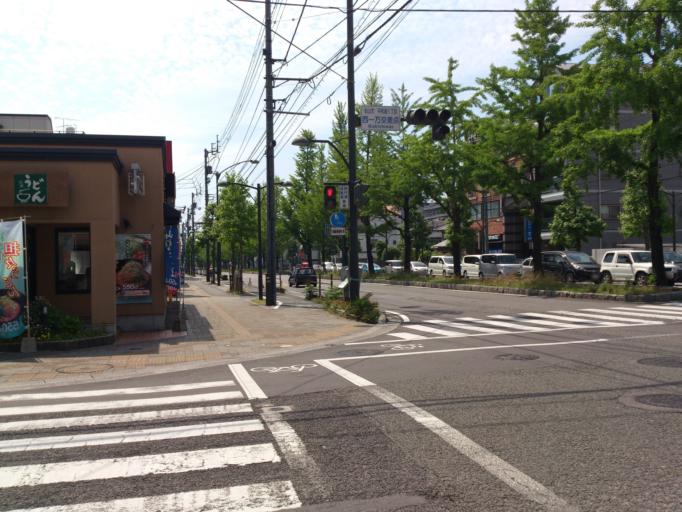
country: JP
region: Ehime
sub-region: Shikoku-chuo Shi
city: Matsuyama
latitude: 33.8474
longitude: 132.7730
